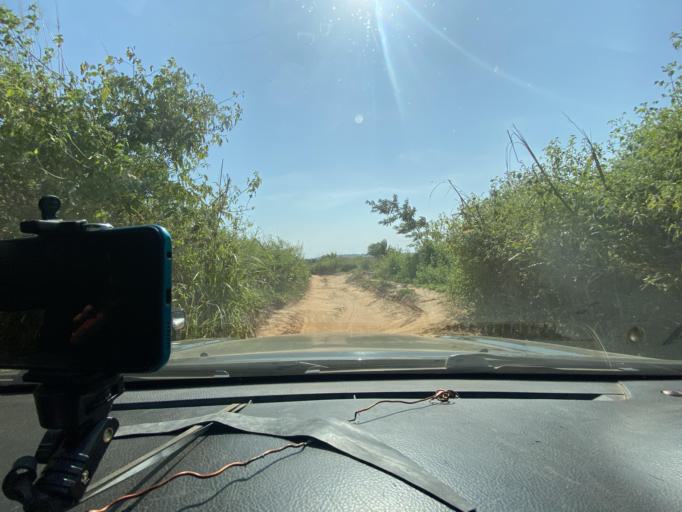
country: CD
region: Kasai-Oriental
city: Kabinda
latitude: -6.1072
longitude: 24.5357
